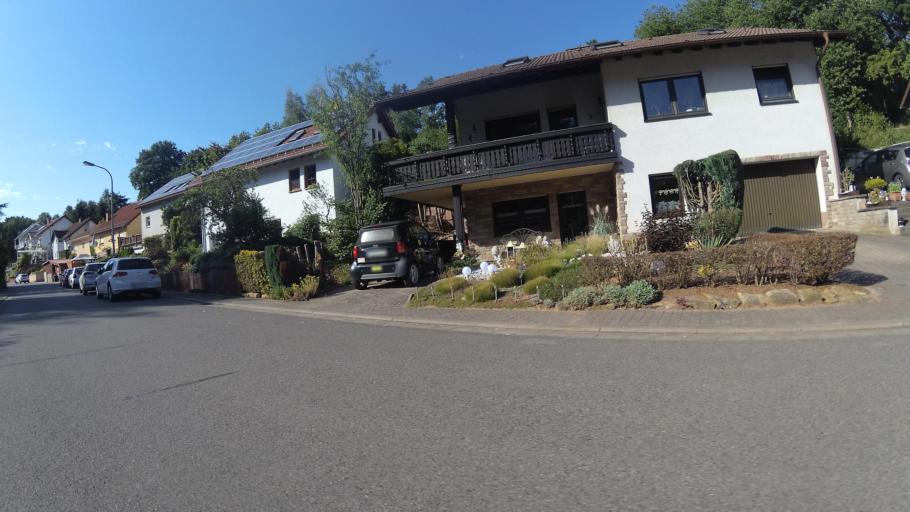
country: DE
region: Rheinland-Pfalz
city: Althornbach
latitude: 49.2111
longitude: 7.3299
